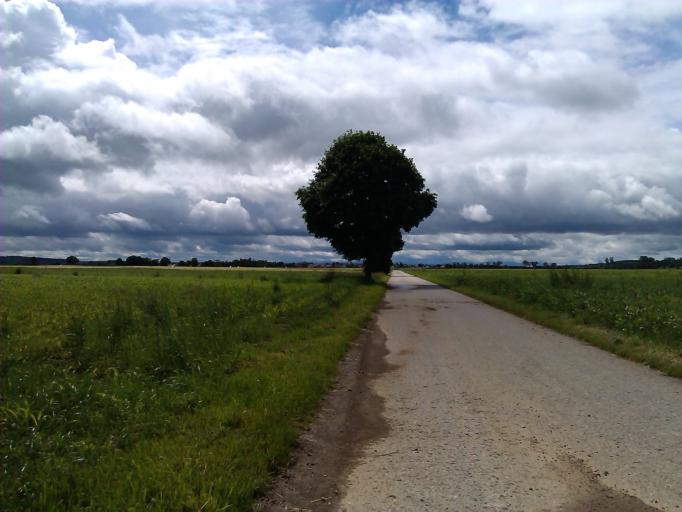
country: DE
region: Bavaria
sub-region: Swabia
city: Bad Worishofen
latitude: 47.9865
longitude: 10.6089
